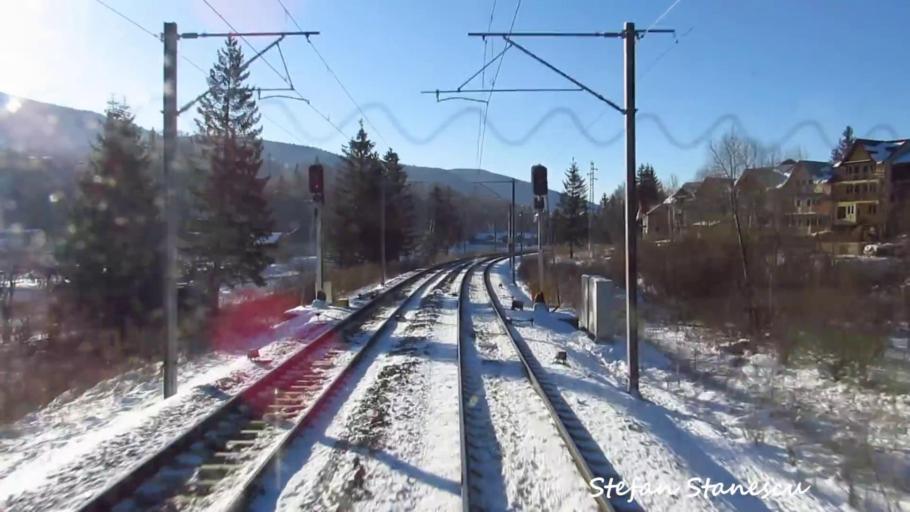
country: RO
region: Prahova
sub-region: Oras Busteni
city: Poiana Tapului
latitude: 45.3849
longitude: 25.5405
